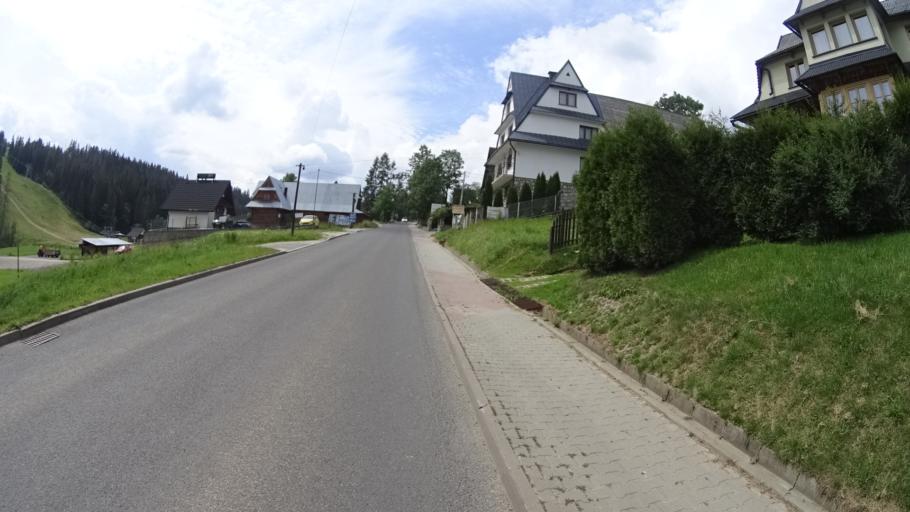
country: PL
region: Lesser Poland Voivodeship
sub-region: Powiat tatrzanski
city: Poronin
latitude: 49.3369
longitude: 19.9832
